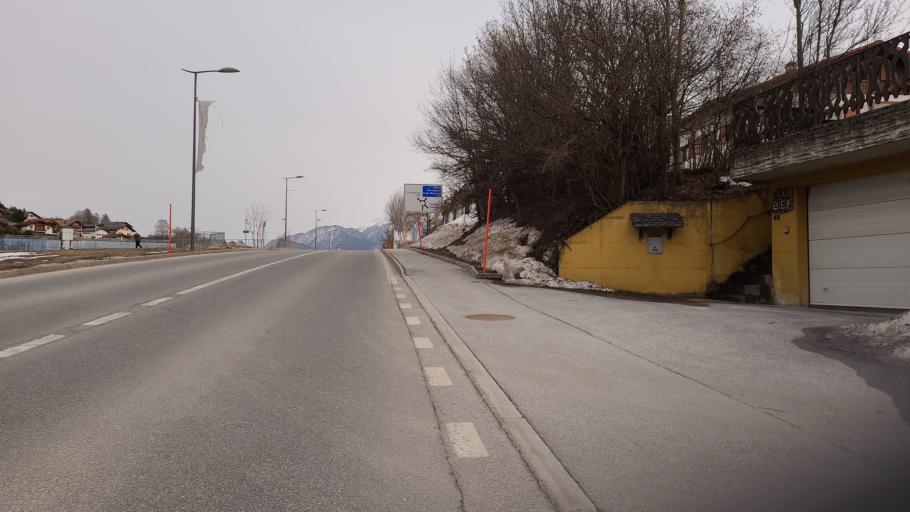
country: CH
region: Valais
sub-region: Sierre District
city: Lens
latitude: 46.2817
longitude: 7.4448
